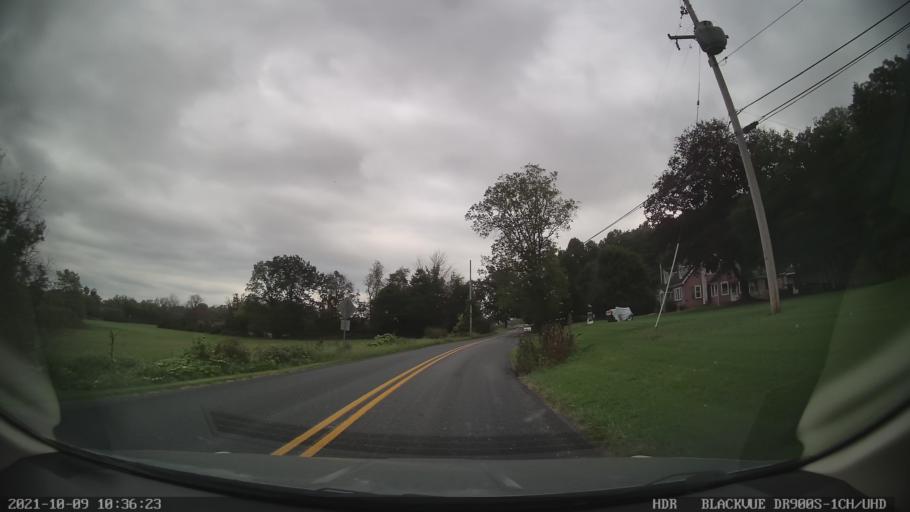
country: US
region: Pennsylvania
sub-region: Berks County
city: Red Lion
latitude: 40.4973
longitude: -75.6434
